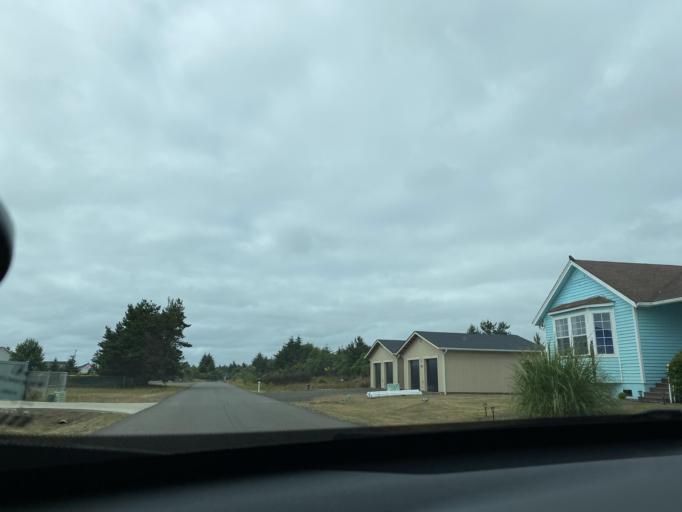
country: US
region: Washington
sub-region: Grays Harbor County
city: Ocean Shores
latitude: 46.9504
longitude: -124.1419
